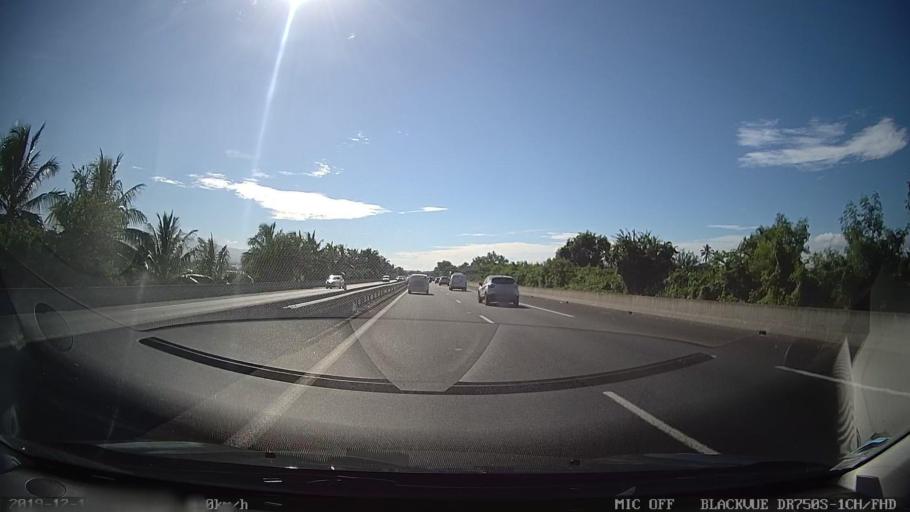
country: RE
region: Reunion
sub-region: Reunion
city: Saint-Louis
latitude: -21.2799
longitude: 55.3858
